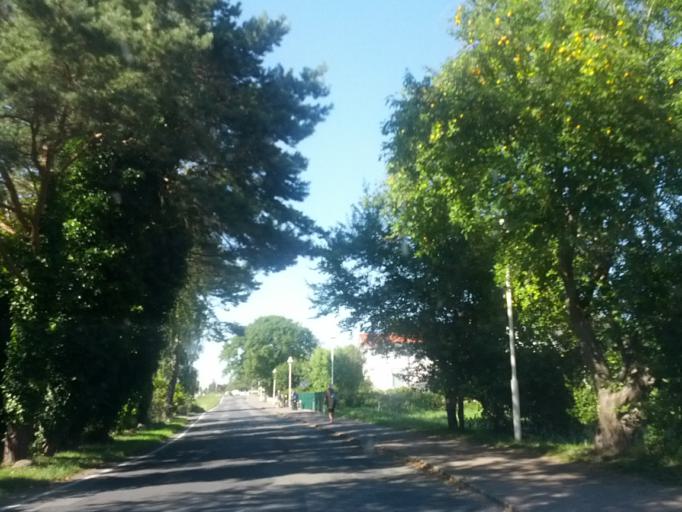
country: DE
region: Mecklenburg-Vorpommern
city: Ostseebad Gohren
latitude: 54.2771
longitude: 13.7151
